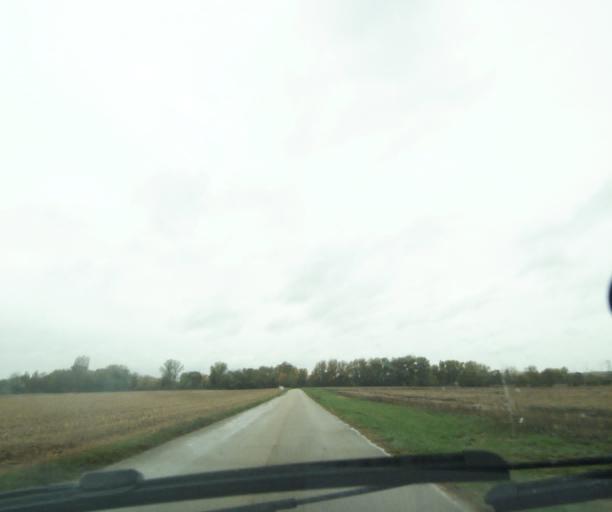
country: FR
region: Rhone-Alpes
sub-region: Departement de l'Ain
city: Saint-Jean-de-Niost
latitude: 45.8089
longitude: 5.2289
